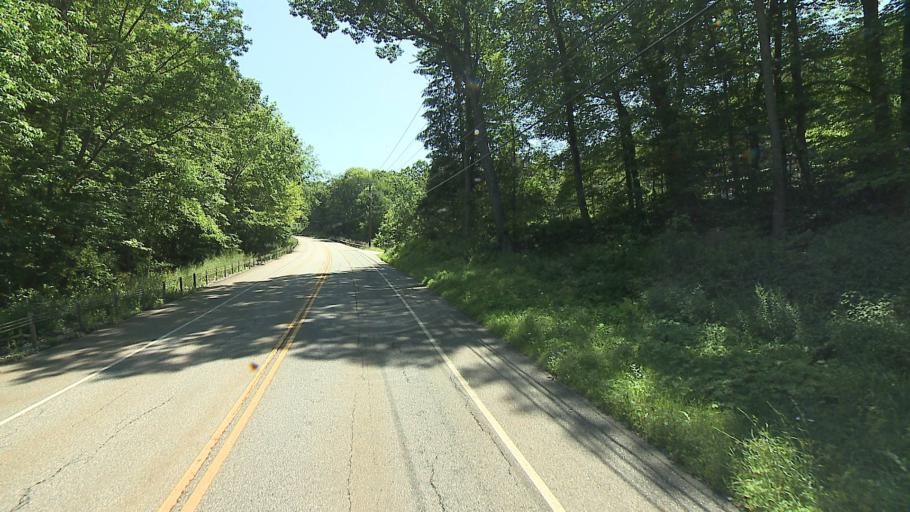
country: US
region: Connecticut
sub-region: Litchfield County
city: Litchfield
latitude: 41.8434
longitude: -73.3018
